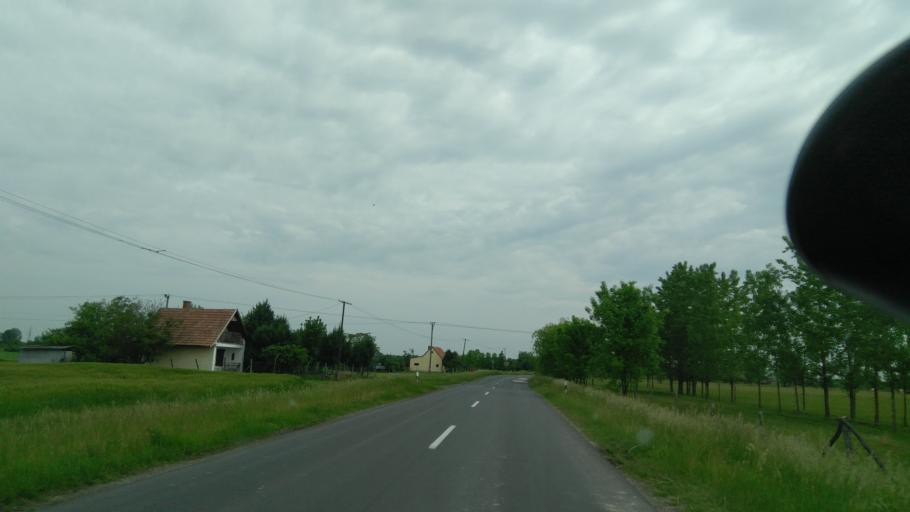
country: HU
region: Bekes
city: Szeghalom
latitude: 46.9996
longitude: 21.1741
